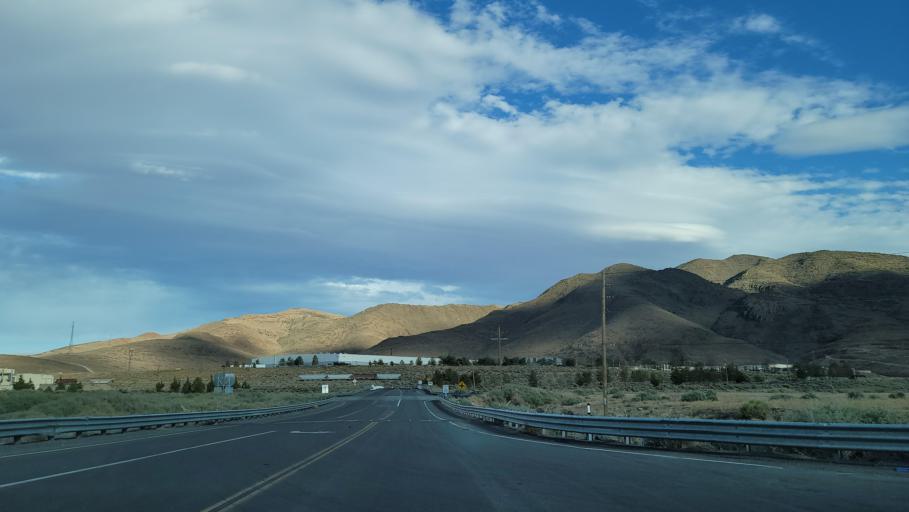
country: US
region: Nevada
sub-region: Washoe County
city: Spanish Springs
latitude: 39.5578
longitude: -119.5548
